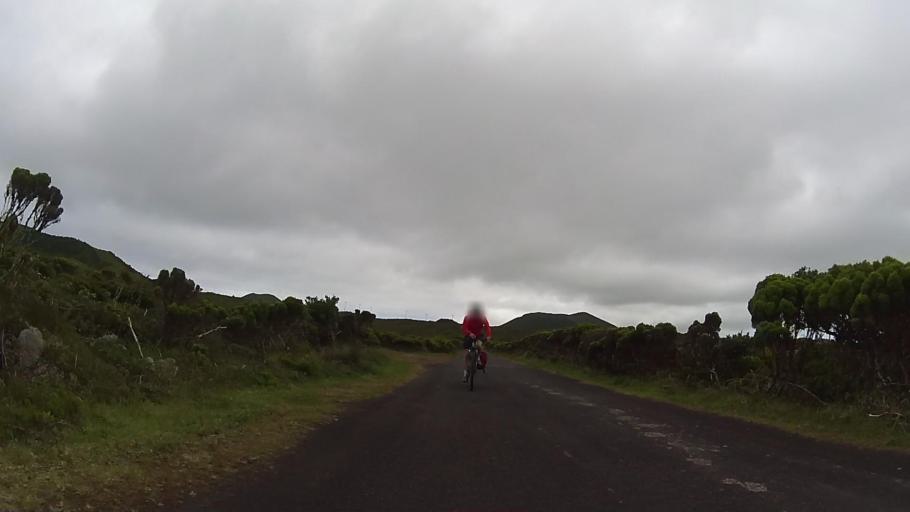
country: PT
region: Azores
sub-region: Sao Roque do Pico
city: Sao Roque do Pico
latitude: 38.4654
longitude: -28.2898
